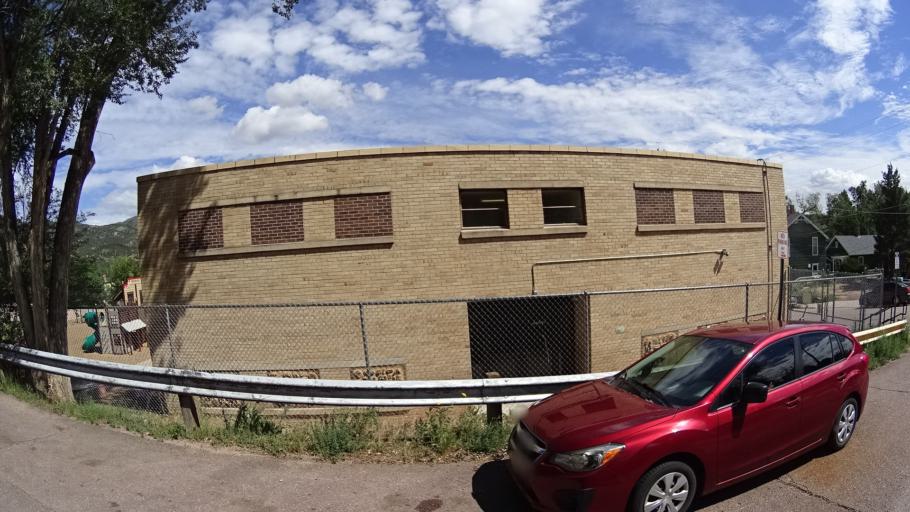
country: US
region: Colorado
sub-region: El Paso County
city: Manitou Springs
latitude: 38.8554
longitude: -104.9145
